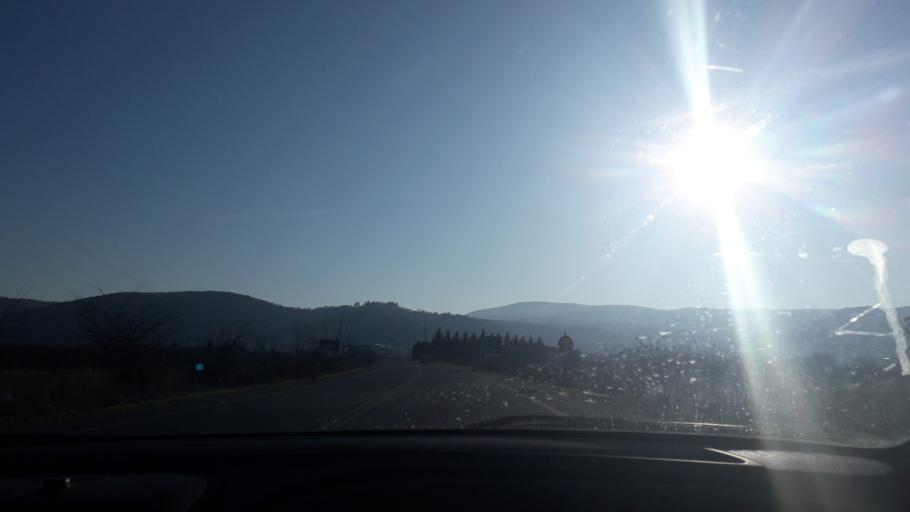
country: GR
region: Central Macedonia
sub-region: Nomos Pellis
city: Apsalos
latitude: 40.8994
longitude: 22.0630
